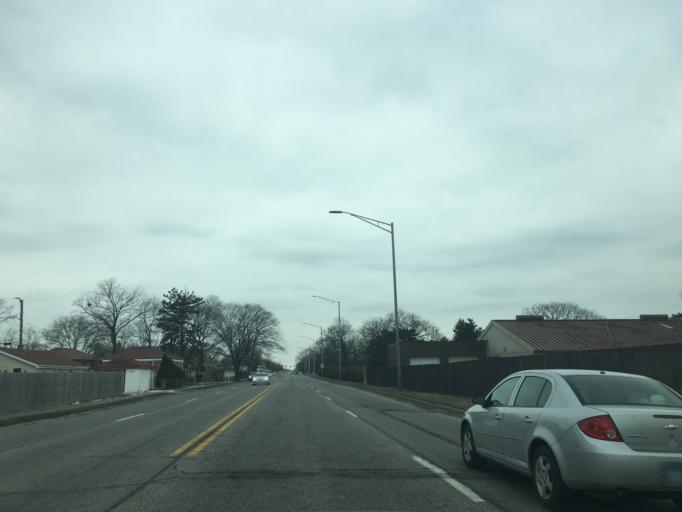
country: US
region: Illinois
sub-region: Cook County
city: North Riverside
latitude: 41.8502
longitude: -87.8170
